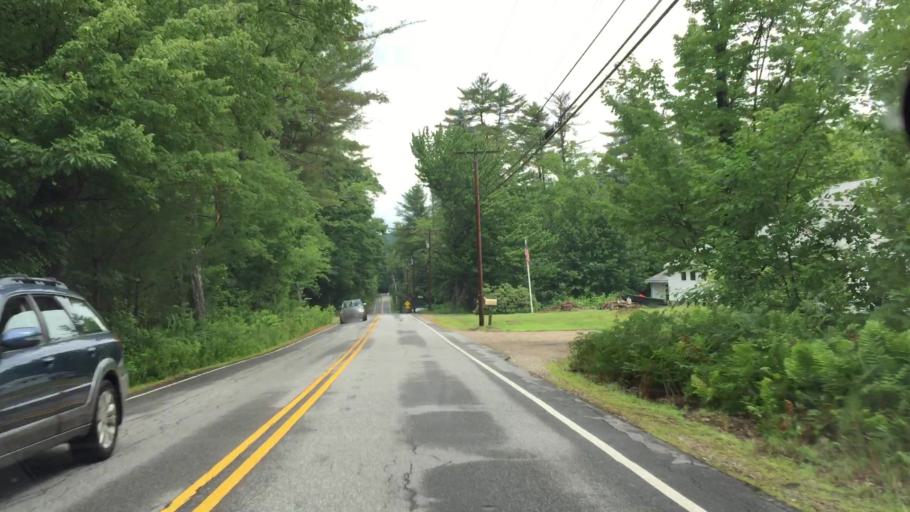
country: US
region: New Hampshire
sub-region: Carroll County
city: Center Harbor
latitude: 43.7268
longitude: -71.4758
